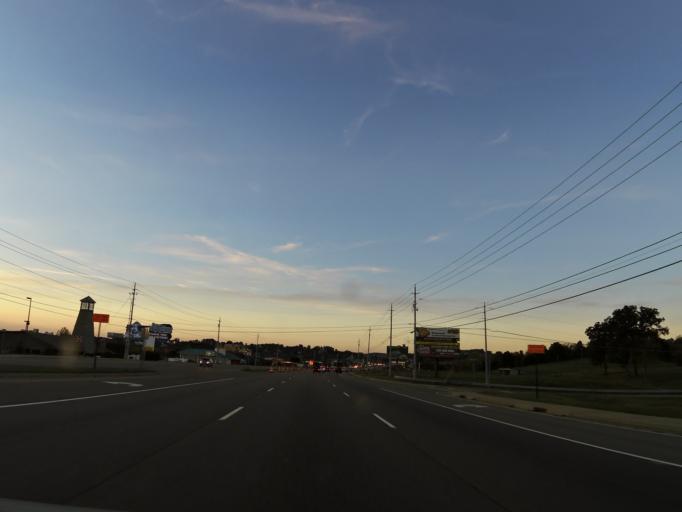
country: US
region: Tennessee
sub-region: Sevier County
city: Sevierville
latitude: 35.9237
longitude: -83.5816
